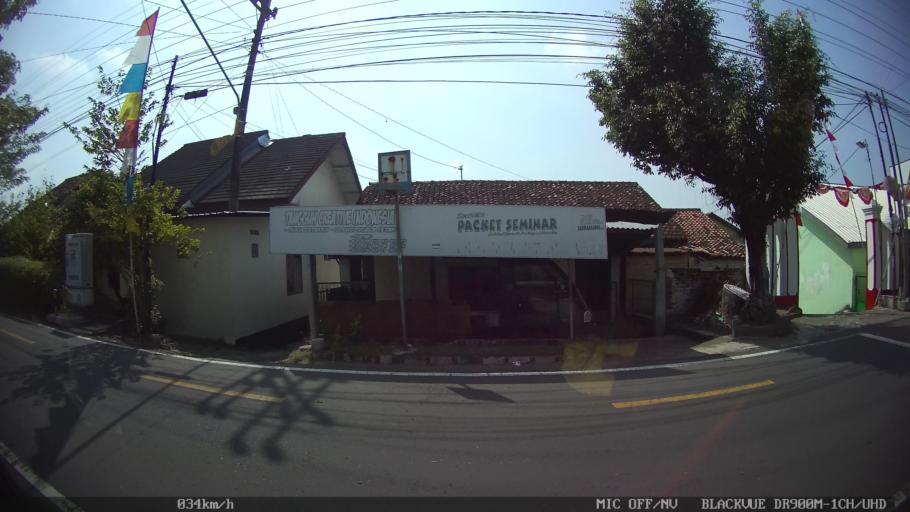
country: ID
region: Daerah Istimewa Yogyakarta
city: Yogyakarta
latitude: -7.8111
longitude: 110.3930
